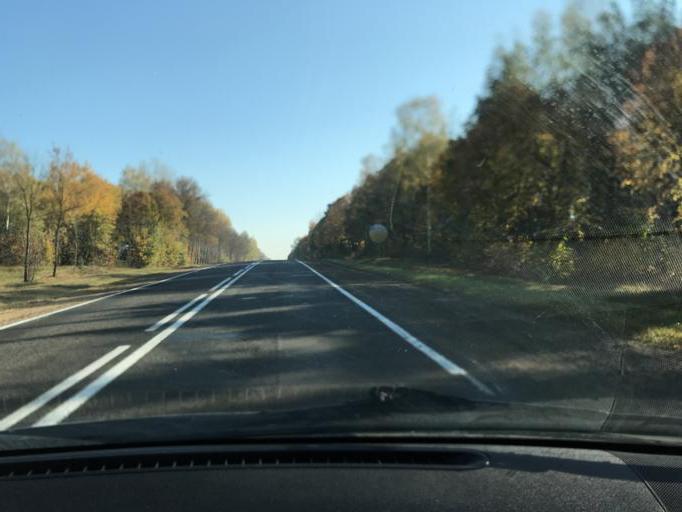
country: BY
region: Minsk
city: Klyetsk
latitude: 52.9645
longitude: 26.5028
